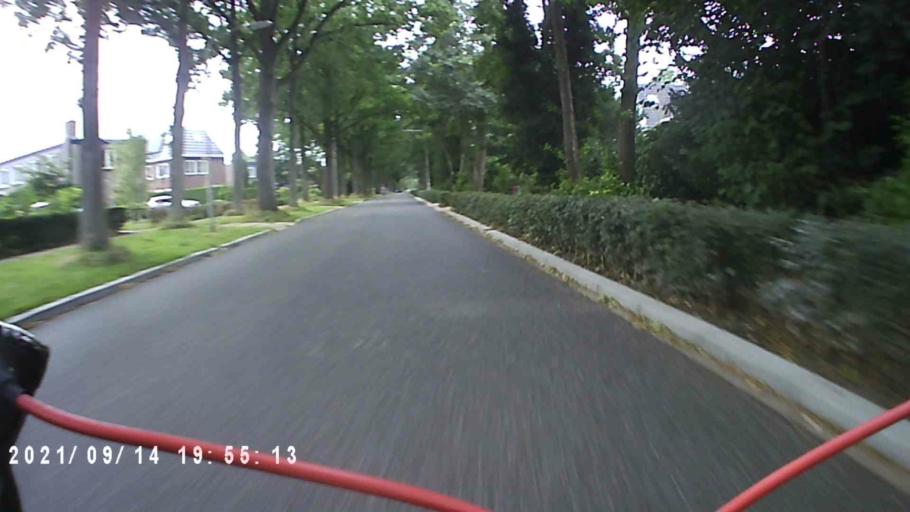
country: NL
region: Groningen
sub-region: Gemeente Haren
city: Haren
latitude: 53.1771
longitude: 6.6115
